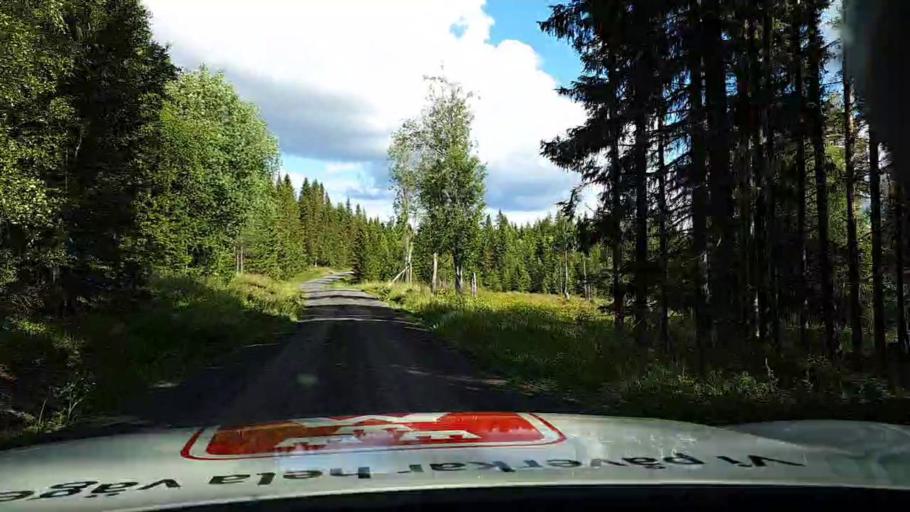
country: SE
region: Jaemtland
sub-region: Krokoms Kommun
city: Valla
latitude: 63.3180
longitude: 13.7679
